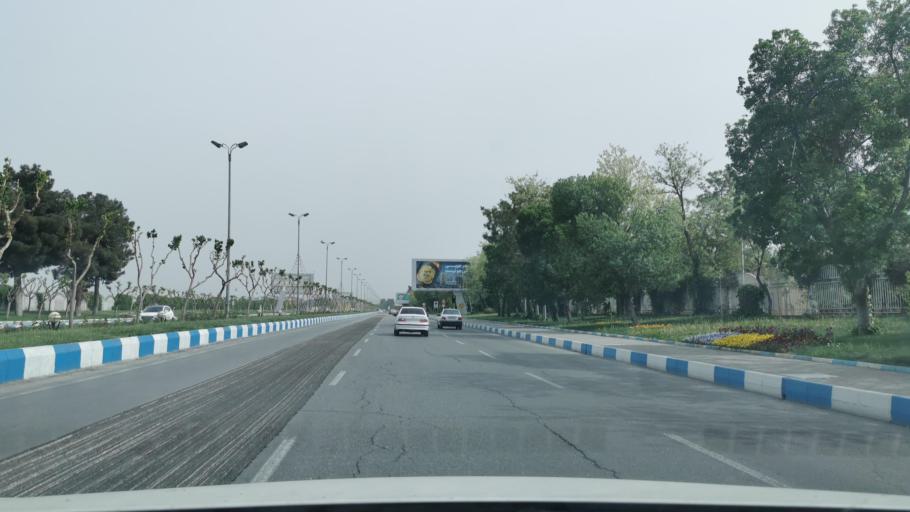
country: IR
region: Razavi Khorasan
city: Mashhad
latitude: 36.2395
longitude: 59.6271
